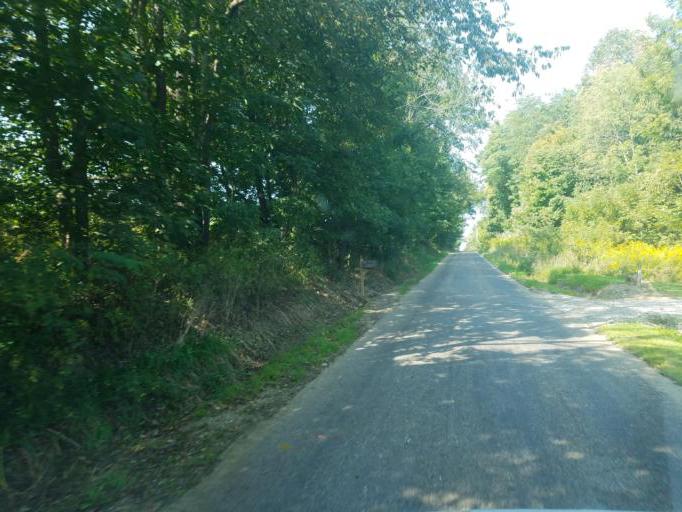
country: US
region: Ohio
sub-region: Knox County
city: Fredericktown
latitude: 40.4834
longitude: -82.5891
